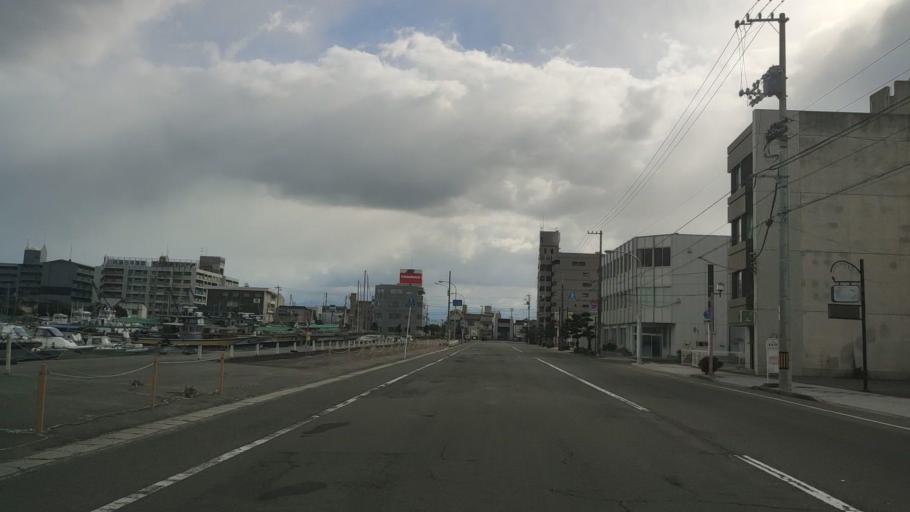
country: JP
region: Ehime
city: Saijo
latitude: 34.0673
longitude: 133.0056
